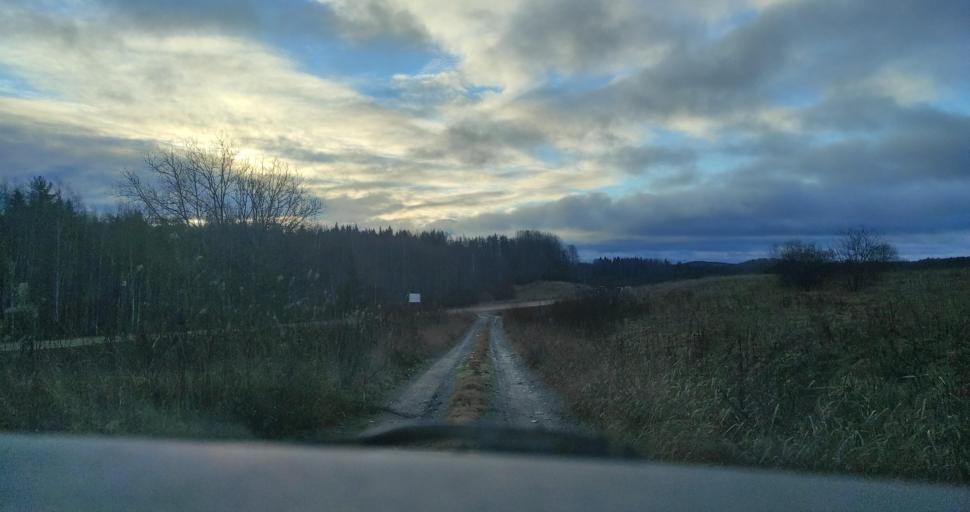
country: RU
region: Republic of Karelia
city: Pitkyaranta
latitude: 61.7266
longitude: 31.3838
